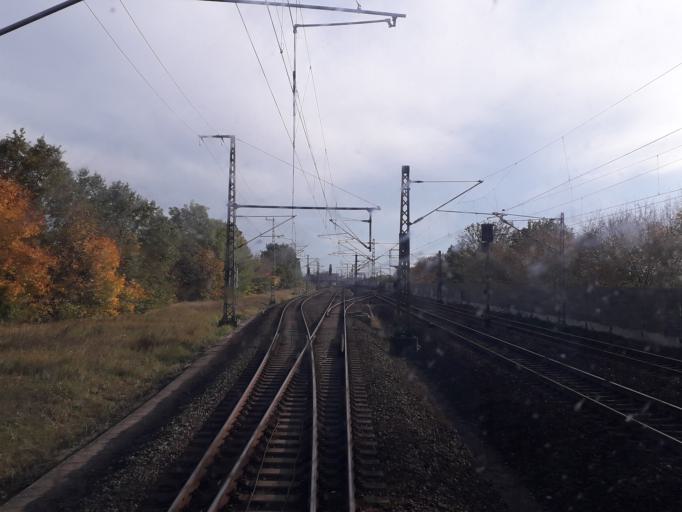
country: DE
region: Brandenburg
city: Wittenberge
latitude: 53.0109
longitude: 11.7613
